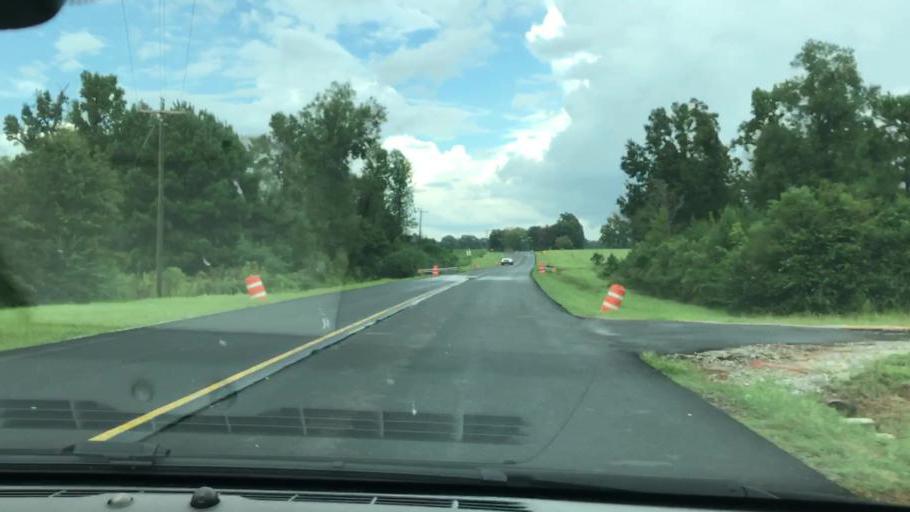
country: US
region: Georgia
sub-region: Early County
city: Blakely
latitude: 31.4248
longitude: -84.9660
